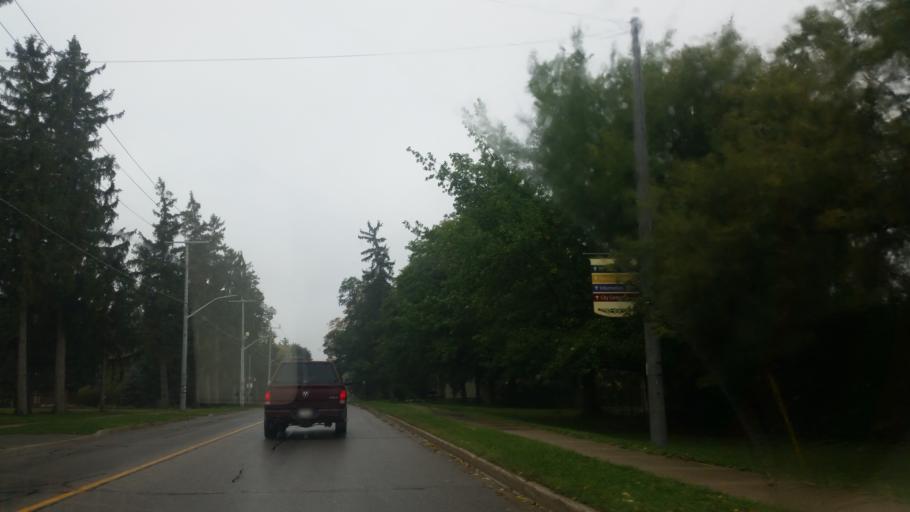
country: CA
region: Ontario
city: Stratford
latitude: 43.3824
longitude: -80.9736
